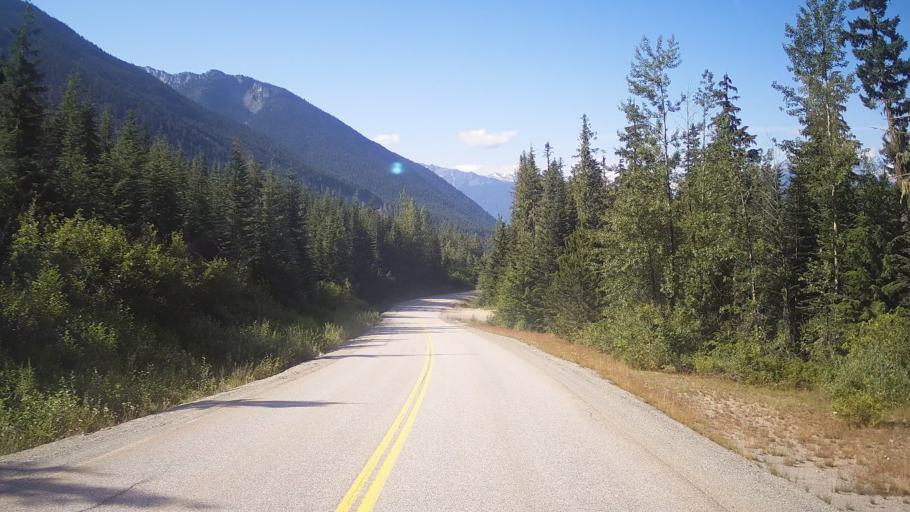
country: CA
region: British Columbia
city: Pemberton
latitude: 50.3550
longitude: -122.5295
